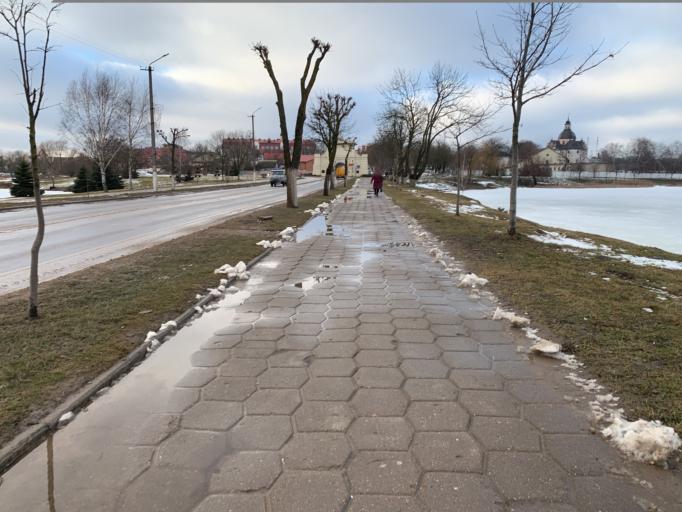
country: BY
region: Minsk
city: Nyasvizh
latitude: 53.2172
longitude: 26.6876
